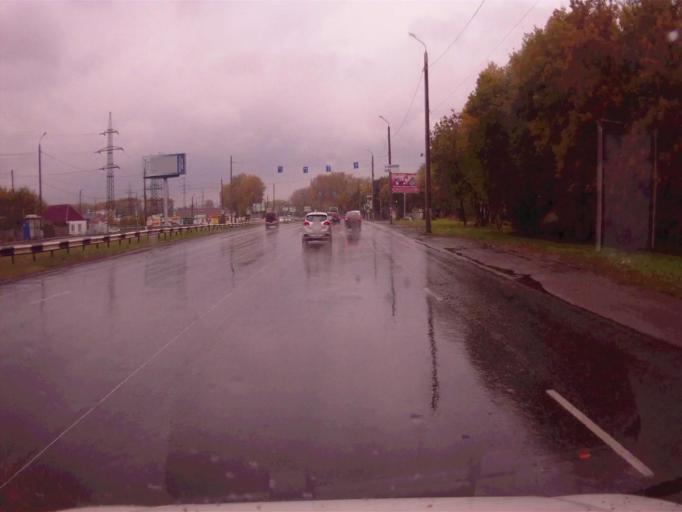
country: RU
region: Chelyabinsk
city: Dolgoderevenskoye
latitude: 55.2394
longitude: 61.3613
